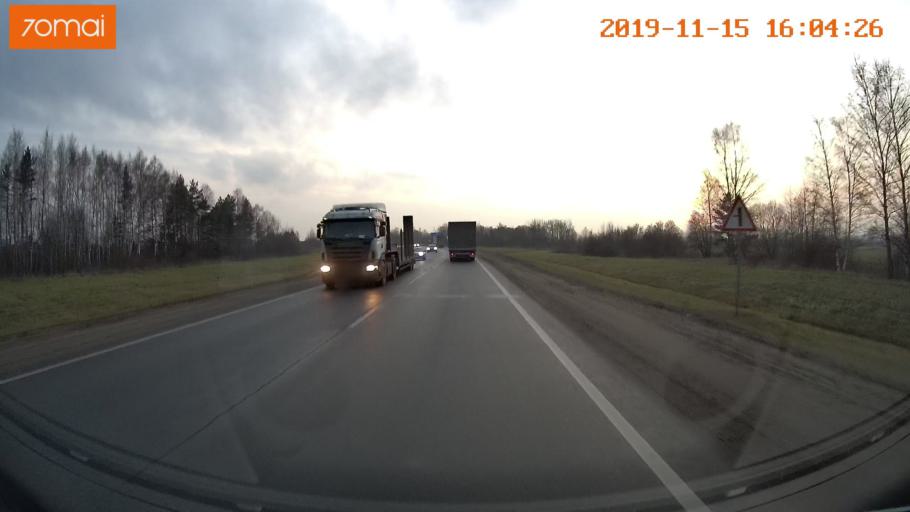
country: RU
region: Jaroslavl
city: Yaroslavl
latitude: 57.7480
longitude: 39.9015
